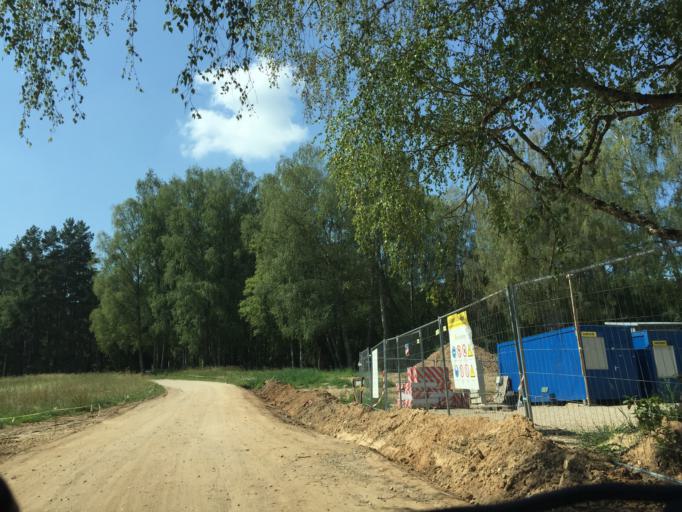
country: LV
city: Tervete
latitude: 56.4949
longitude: 23.4071
